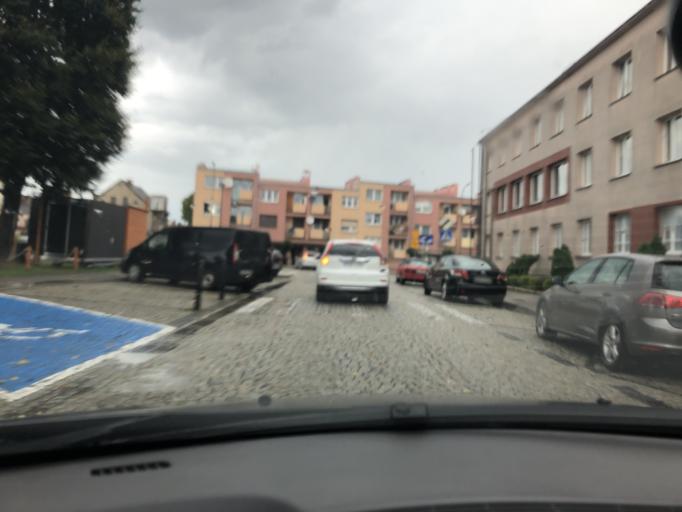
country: PL
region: Lodz Voivodeship
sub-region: Powiat wieruszowski
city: Wieruszow
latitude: 51.2950
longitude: 18.1516
